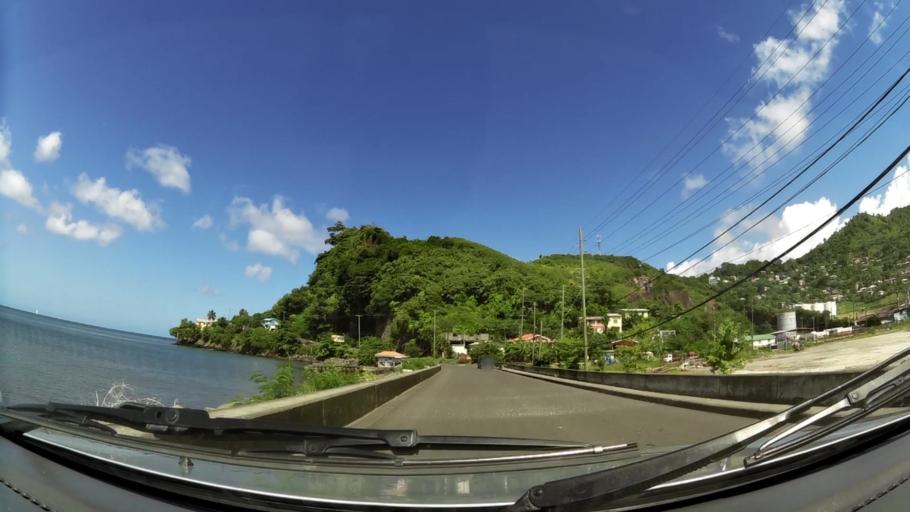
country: GD
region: Saint George
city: Saint George's
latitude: 12.0603
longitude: -61.7547
